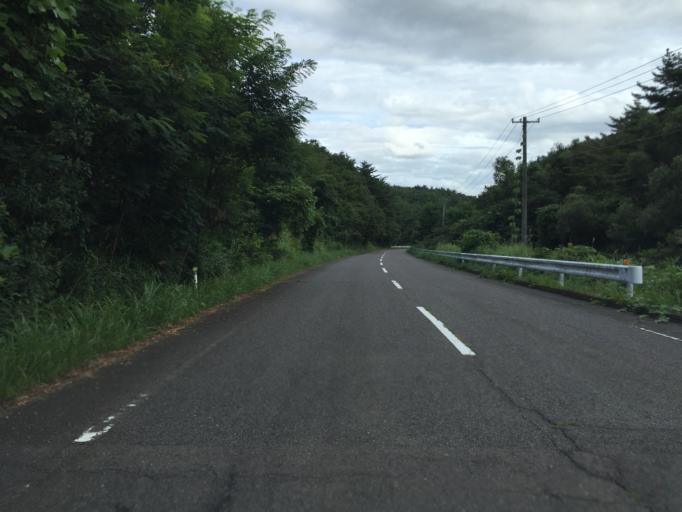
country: JP
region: Fukushima
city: Motomiya
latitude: 37.5453
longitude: 140.3189
